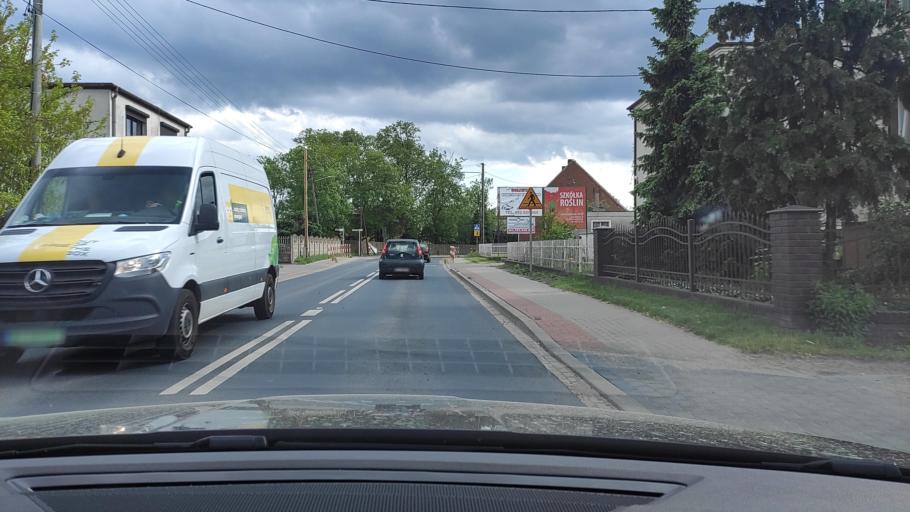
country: PL
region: Greater Poland Voivodeship
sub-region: Powiat poznanski
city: Swarzedz
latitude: 52.3826
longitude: 17.0735
